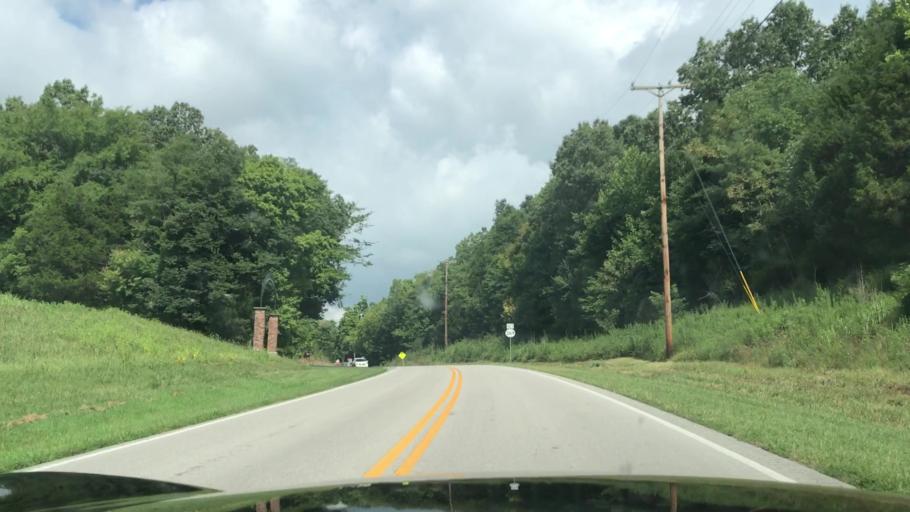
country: US
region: Kentucky
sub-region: Ohio County
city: Oak Grove
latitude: 37.2058
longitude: -86.8889
